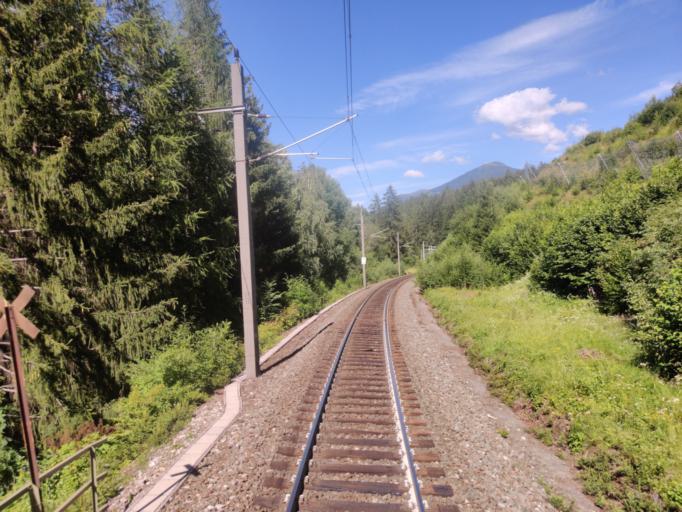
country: AT
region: Tyrol
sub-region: Politischer Bezirk Landeck
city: Pians
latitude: 47.1321
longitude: 10.5162
